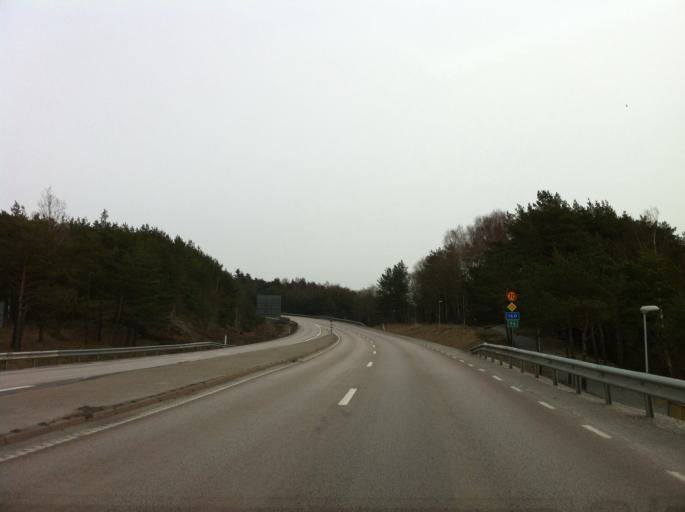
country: SE
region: Vaestra Goetaland
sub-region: Tjorns Kommun
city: Myggenas
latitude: 58.0535
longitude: 11.7571
